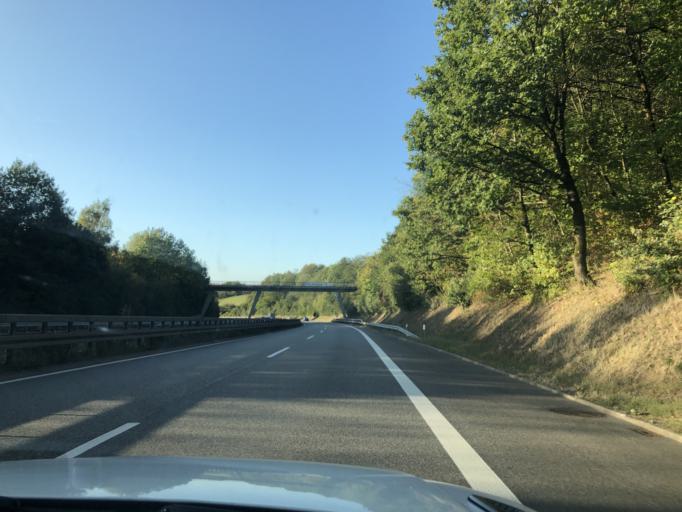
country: DE
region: Saarland
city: Eppelborn
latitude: 49.4262
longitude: 6.9715
